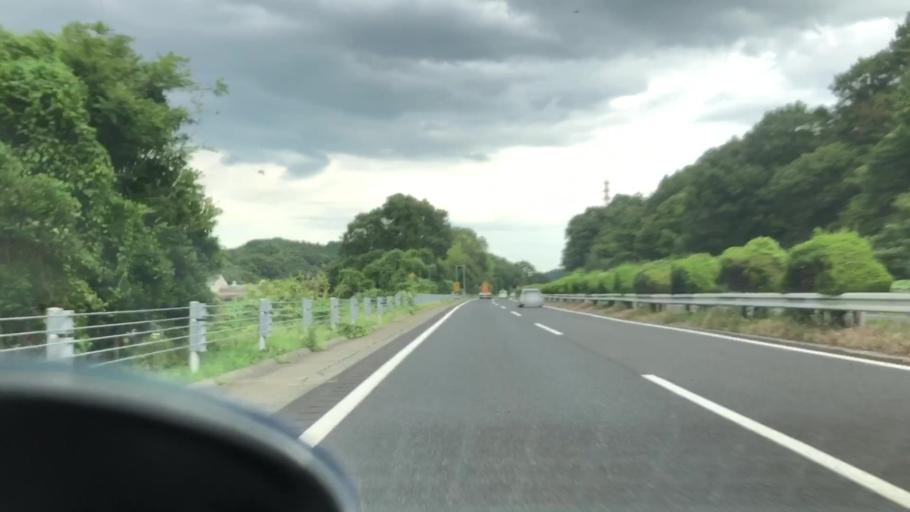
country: JP
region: Hyogo
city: Himeji
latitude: 34.9559
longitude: 134.7175
